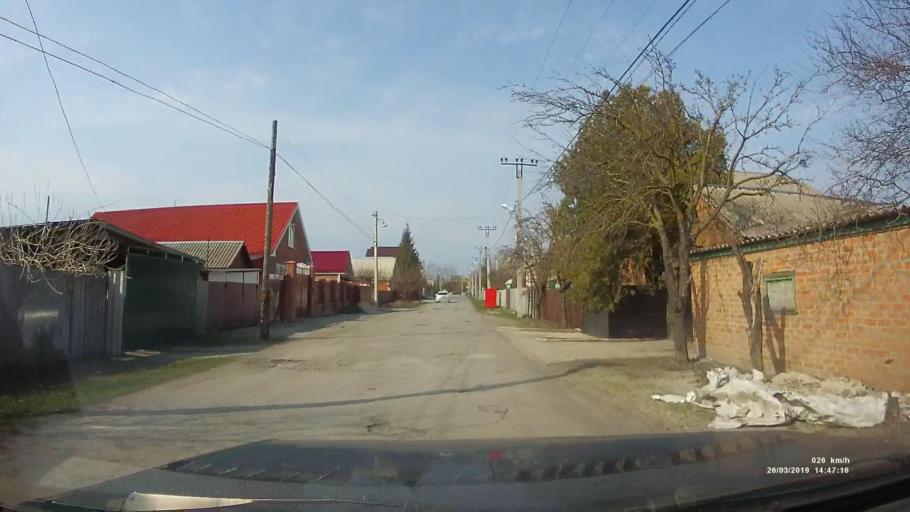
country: RU
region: Rostov
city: Novobessergenovka
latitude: 47.1901
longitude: 38.8593
